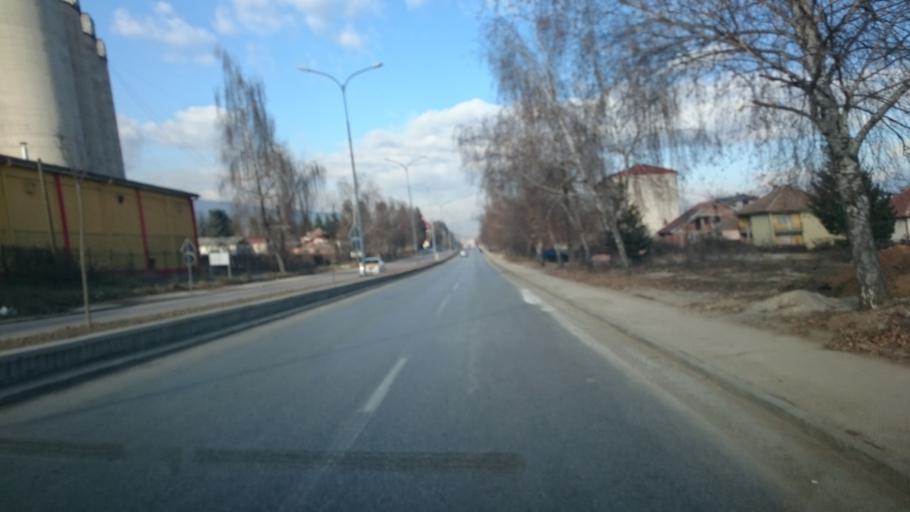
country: MK
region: Kicevo
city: Kicevo
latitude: 41.5016
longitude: 20.9525
